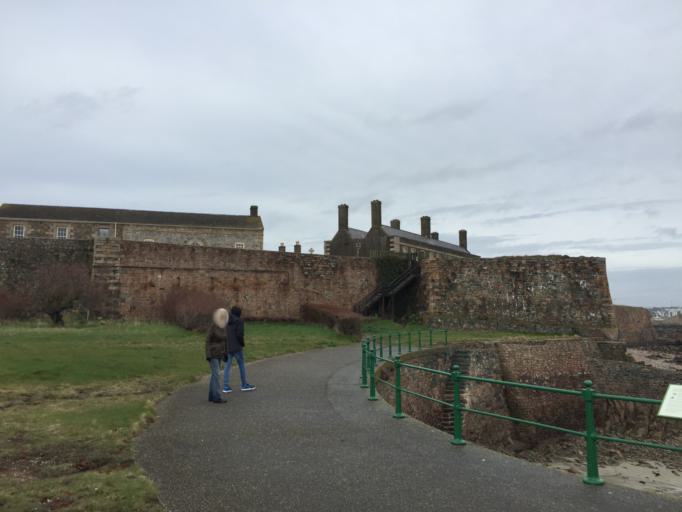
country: JE
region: St Helier
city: Saint Helier
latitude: 49.1752
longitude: -2.1257
